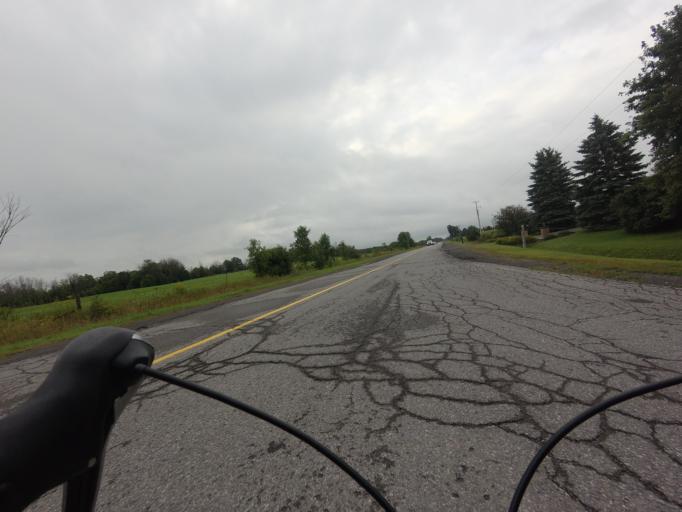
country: CA
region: Ontario
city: Bells Corners
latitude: 45.1628
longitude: -75.7977
